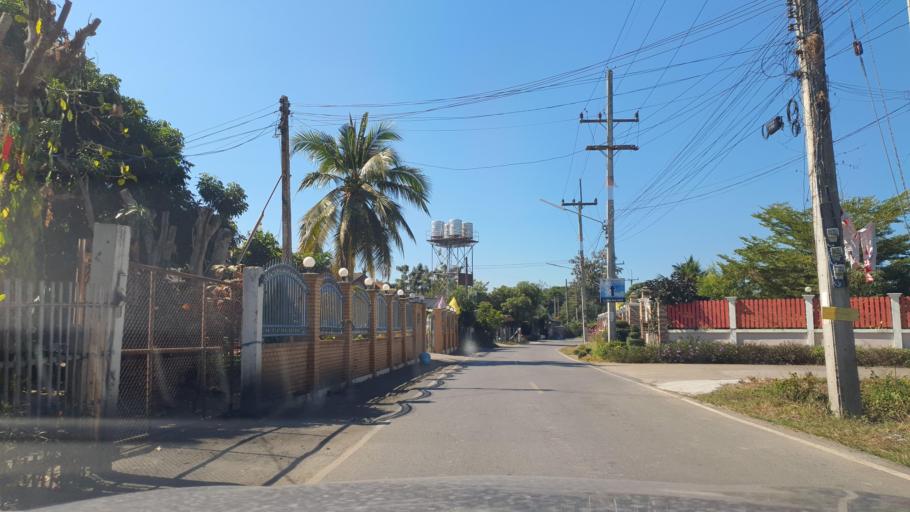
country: TH
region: Chiang Mai
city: San Pa Tong
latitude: 18.6507
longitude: 98.8985
